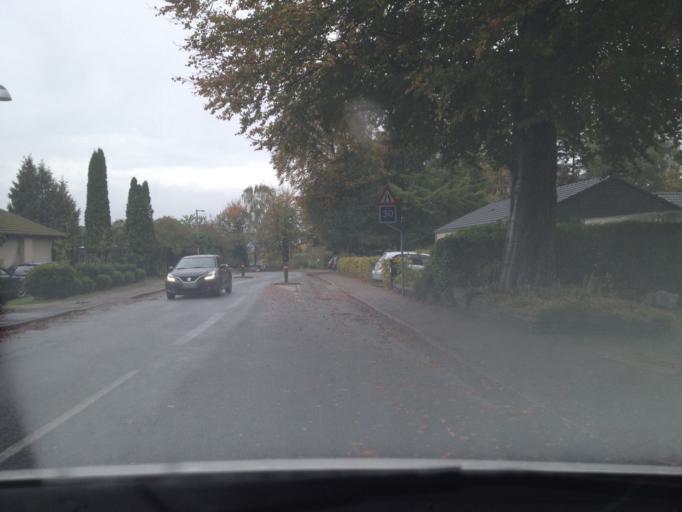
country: DK
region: Capital Region
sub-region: Fredensborg Kommune
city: Fredensborg
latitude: 55.9786
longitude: 12.3932
